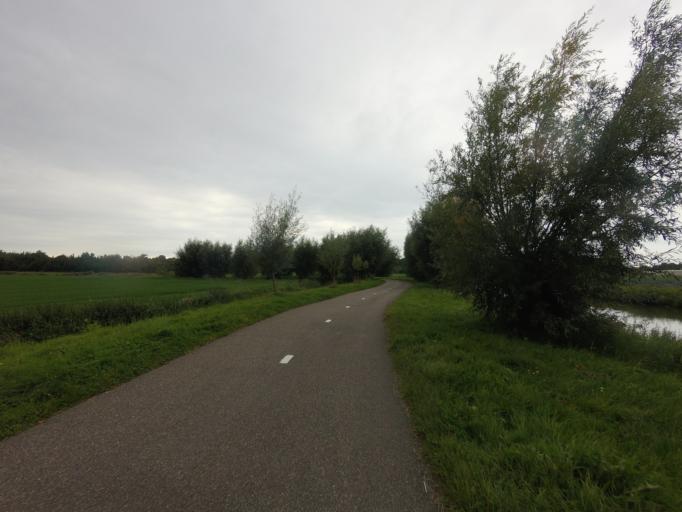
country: NL
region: North Holland
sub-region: Gemeente Enkhuizen
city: Enkhuizen
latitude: 52.7164
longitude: 5.2587
